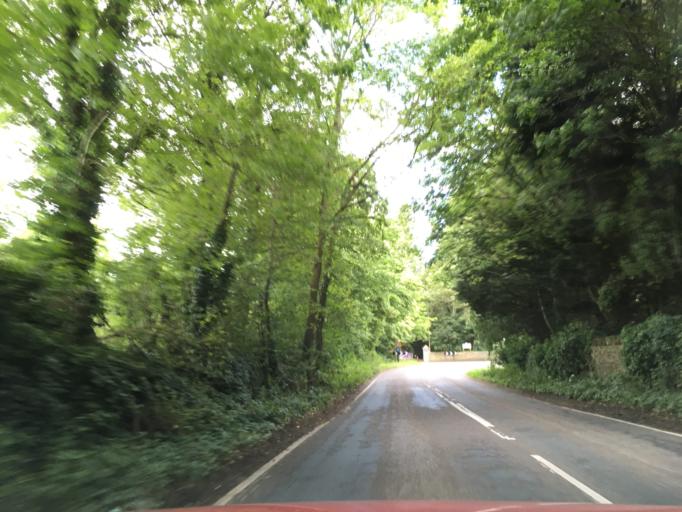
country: GB
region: England
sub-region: Oxfordshire
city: Shipton under Wychwood
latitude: 51.8537
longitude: -1.6015
